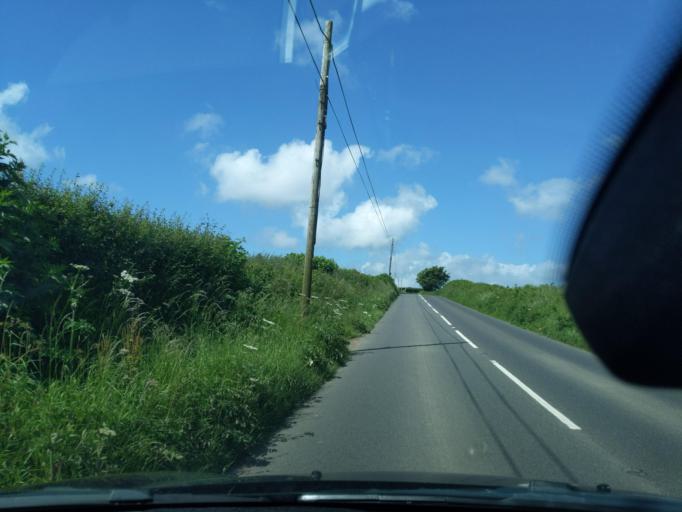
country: GB
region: England
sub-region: Devon
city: Great Torrington
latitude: 50.9722
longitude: -4.1095
